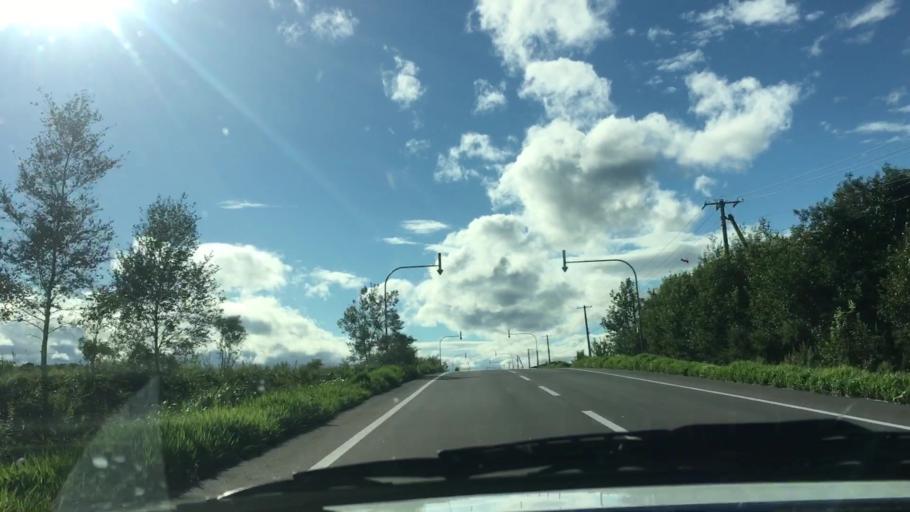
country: JP
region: Hokkaido
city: Otofuke
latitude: 43.1643
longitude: 143.1432
